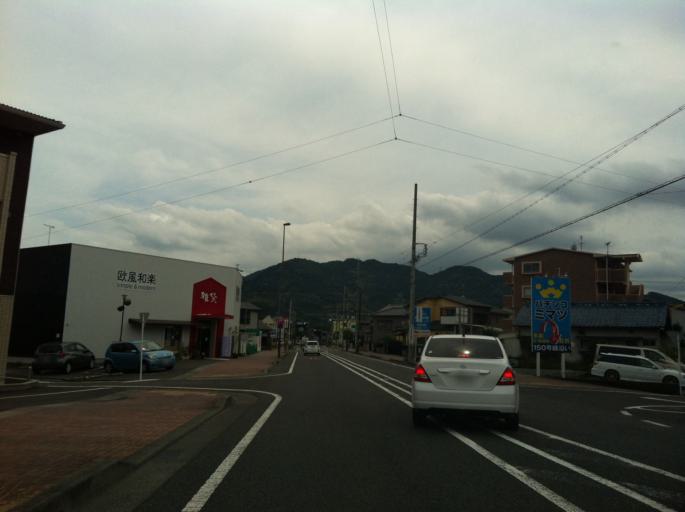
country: JP
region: Shizuoka
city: Shizuoka-shi
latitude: 34.9467
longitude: 138.3690
